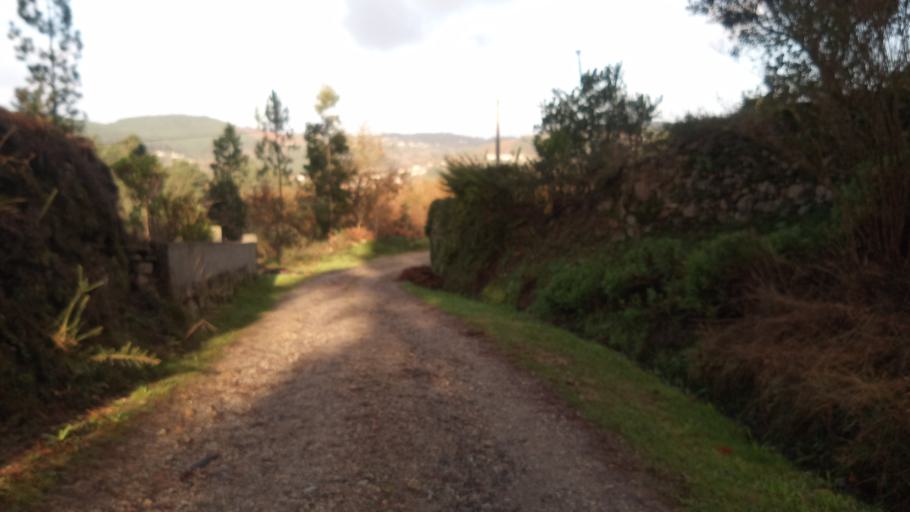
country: PT
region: Viana do Castelo
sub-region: Paredes de Coura
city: Paredes de Coura
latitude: 41.8974
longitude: -8.6148
